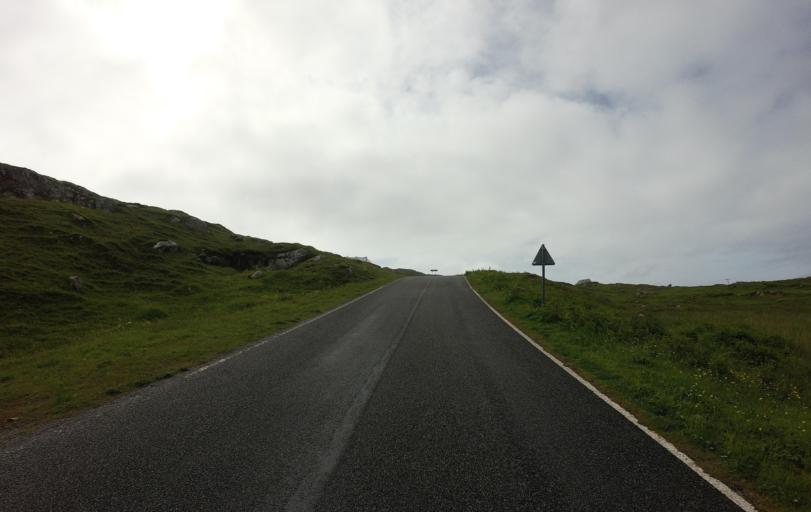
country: GB
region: Scotland
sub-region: Eilean Siar
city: Isle of South Uist
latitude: 57.0813
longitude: -7.3029
